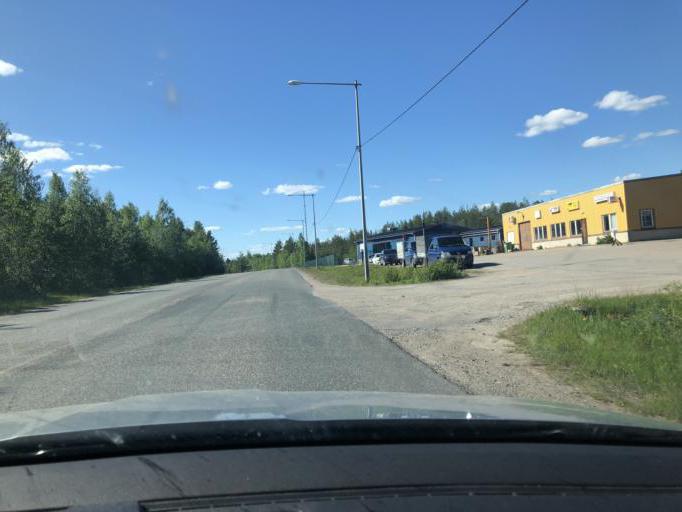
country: SE
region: Norrbotten
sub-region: Kalix Kommun
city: Kalix
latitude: 65.8601
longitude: 23.1590
